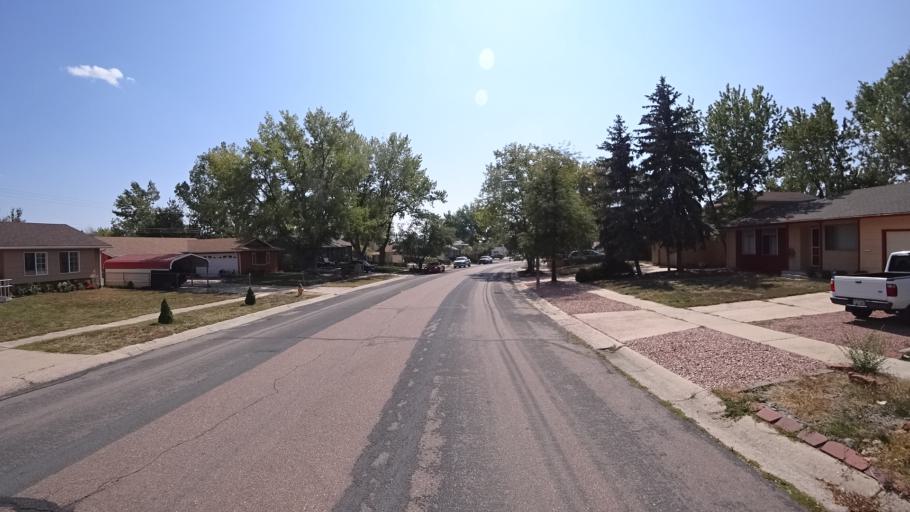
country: US
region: Colorado
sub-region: El Paso County
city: Colorado Springs
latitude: 38.8273
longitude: -104.7694
